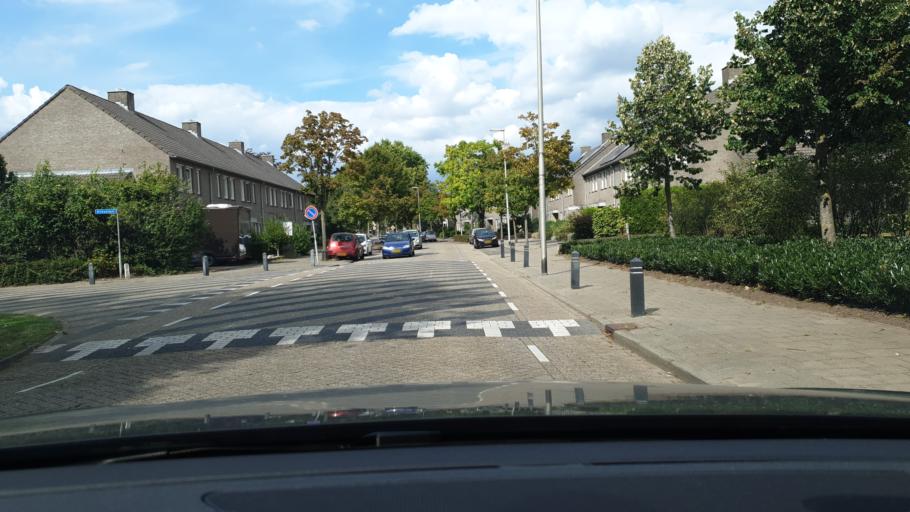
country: NL
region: North Brabant
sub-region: Gemeente Valkenswaard
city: Valkenswaard
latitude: 51.3504
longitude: 5.4274
